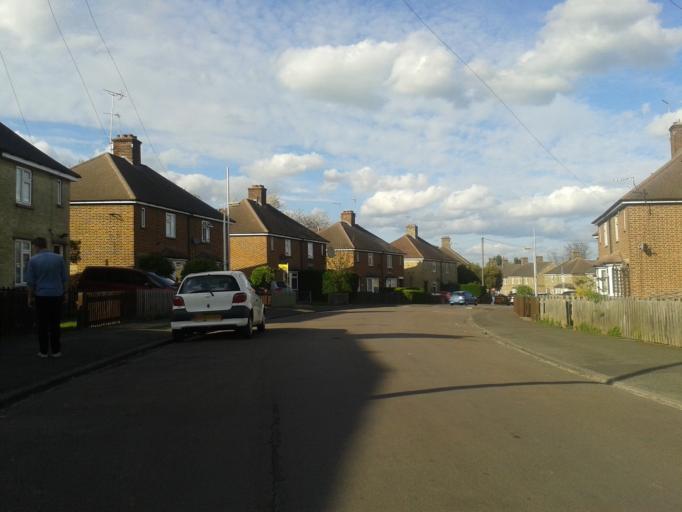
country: GB
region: England
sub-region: Cambridgeshire
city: Cambridge
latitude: 52.2010
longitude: 0.1493
